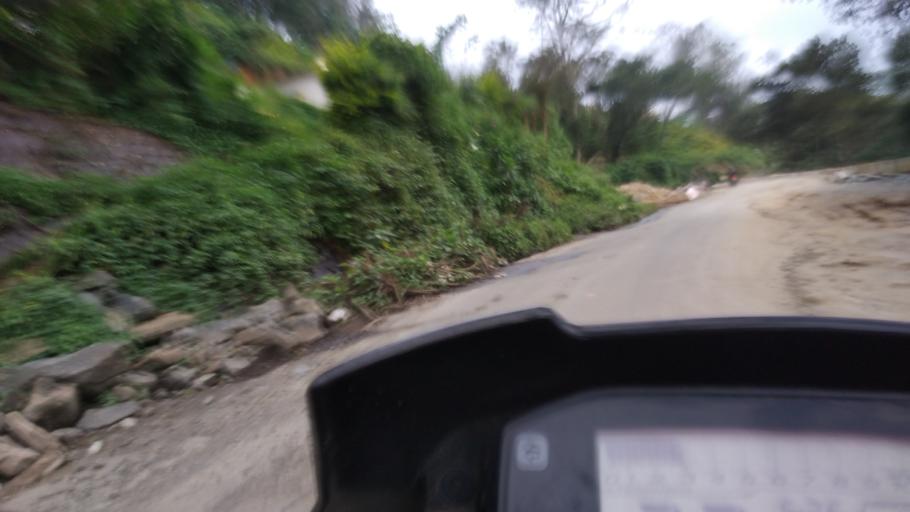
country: IN
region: Tamil Nadu
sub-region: Theni
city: Bodinayakkanur
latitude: 10.0023
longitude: 77.2229
